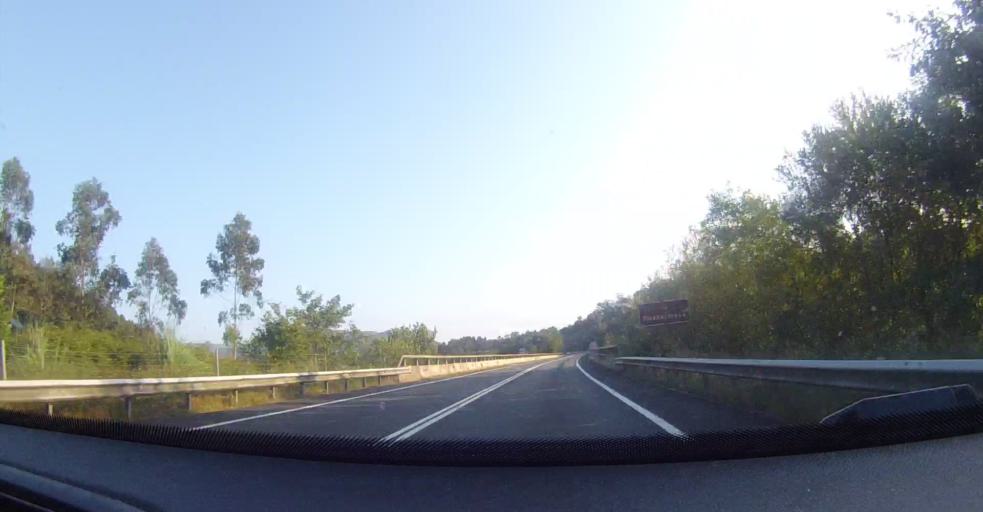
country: ES
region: Cantabria
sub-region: Provincia de Cantabria
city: Ampuero
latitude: 43.3310
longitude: -3.4069
